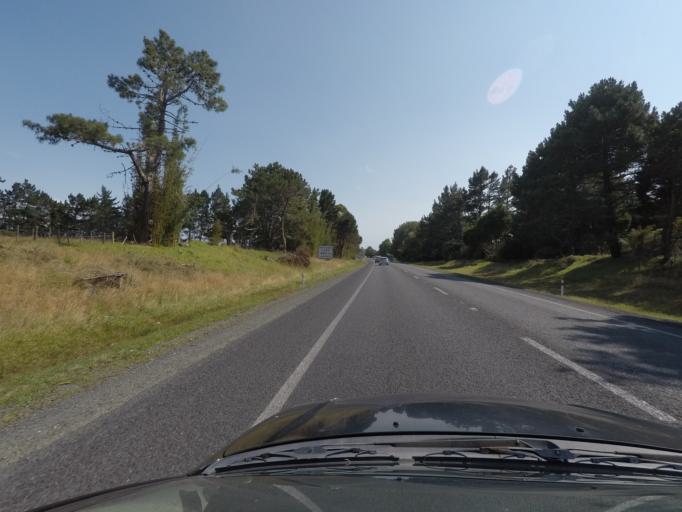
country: NZ
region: Northland
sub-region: Whangarei
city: Ruakaka
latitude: -35.9575
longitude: 174.4506
